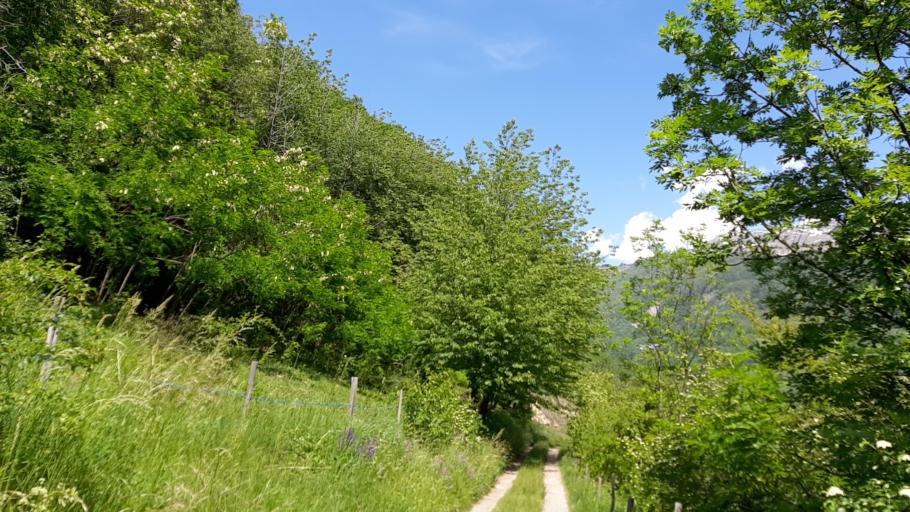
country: FR
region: Rhone-Alpes
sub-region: Departement de la Savoie
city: La Chambre
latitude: 45.3706
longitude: 6.3040
